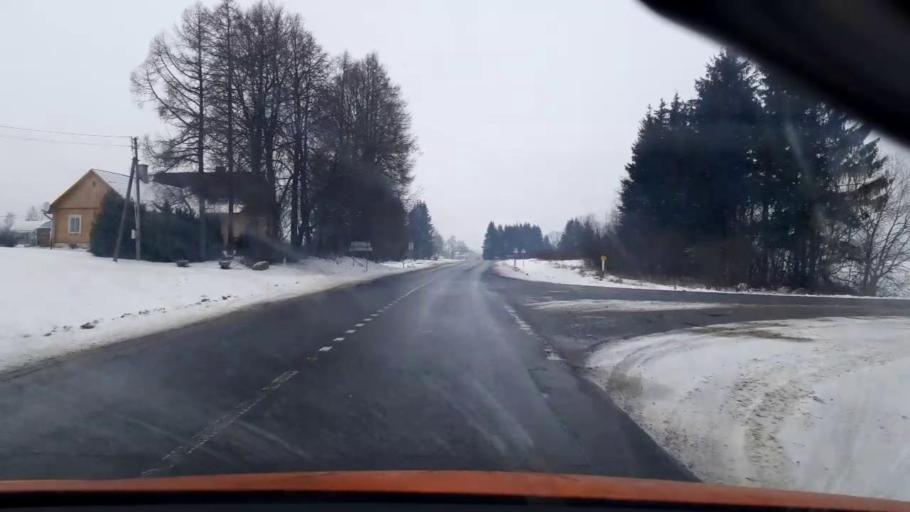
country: LT
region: Vilnius County
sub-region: Vilnius
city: Fabijoniskes
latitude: 54.8693
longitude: 25.2515
